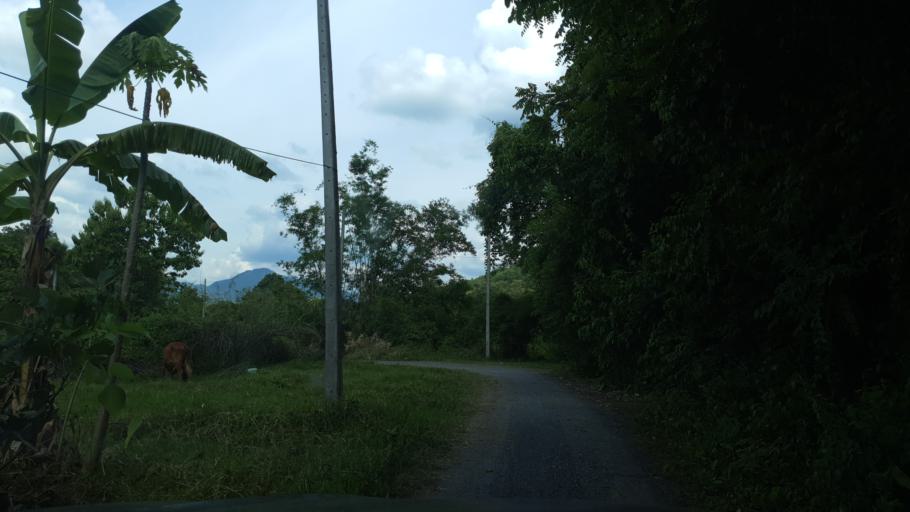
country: TH
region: Chiang Mai
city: San Kamphaeng
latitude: 18.7207
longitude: 99.1861
